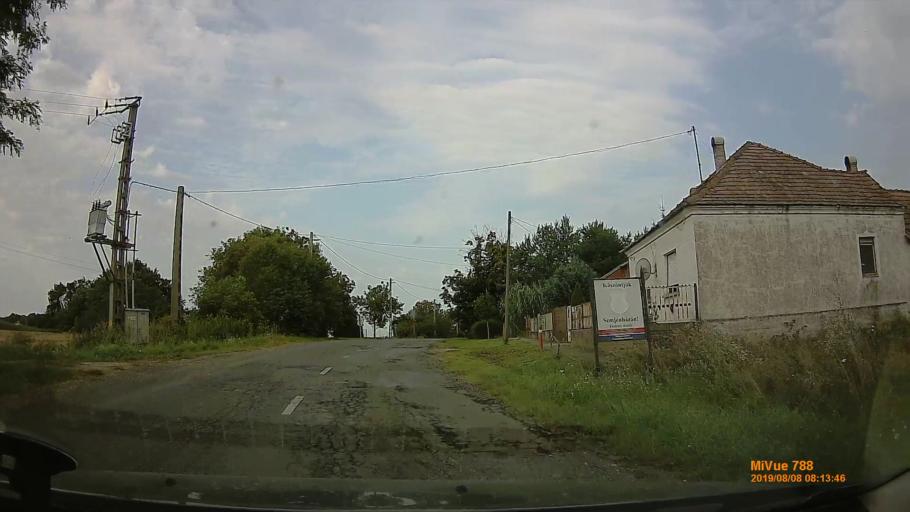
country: HU
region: Zala
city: Murakeresztur
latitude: 46.4022
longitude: 16.8601
